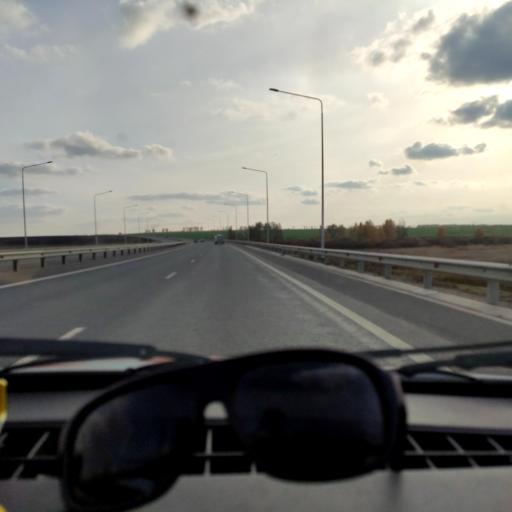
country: RU
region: Bashkortostan
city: Tolbazy
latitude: 54.3077
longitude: 55.8816
